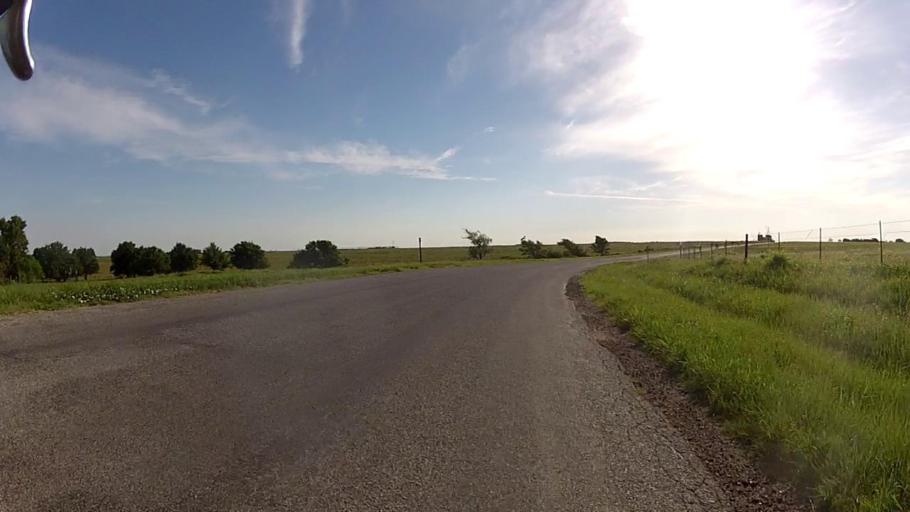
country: US
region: Kansas
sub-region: Cowley County
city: Arkansas City
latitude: 37.0554
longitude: -96.8224
